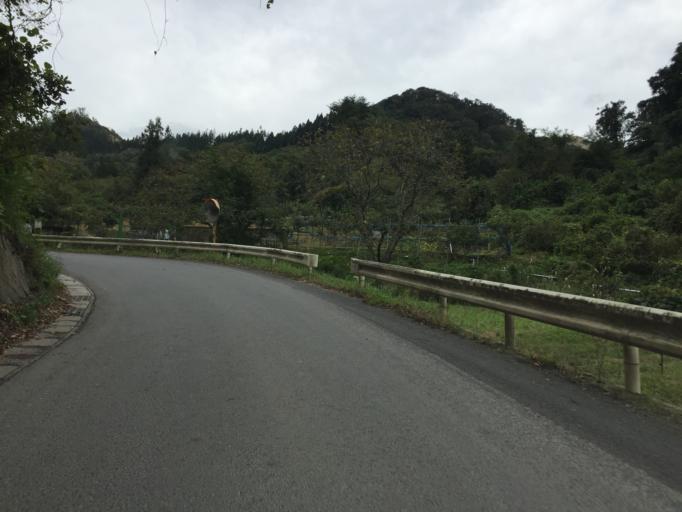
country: JP
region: Fukushima
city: Yanagawamachi-saiwaicho
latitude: 37.8800
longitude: 140.6830
